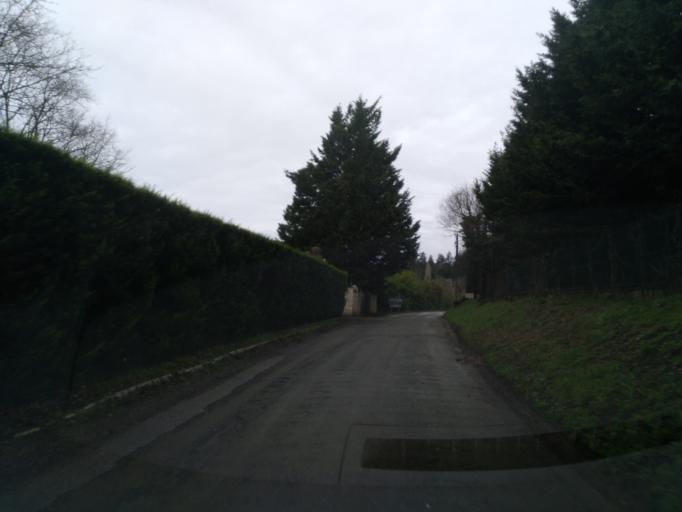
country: FR
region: Ile-de-France
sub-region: Departement des Yvelines
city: Chavenay
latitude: 48.8751
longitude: 1.9979
